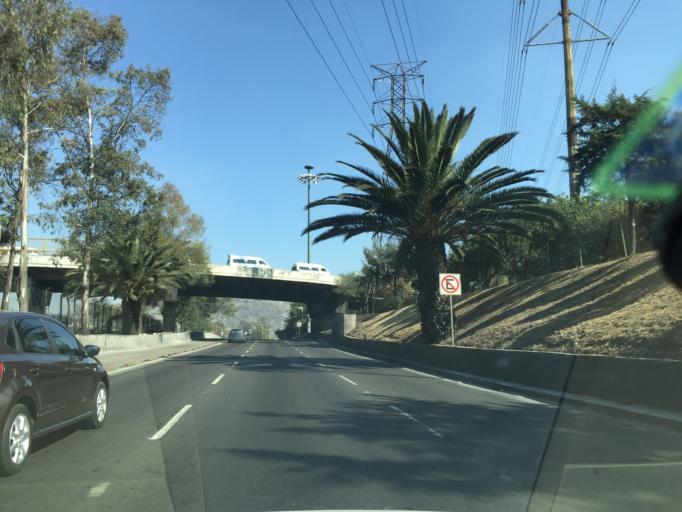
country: MX
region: Mexico
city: Colonia Lindavista
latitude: 19.4921
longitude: -99.1202
